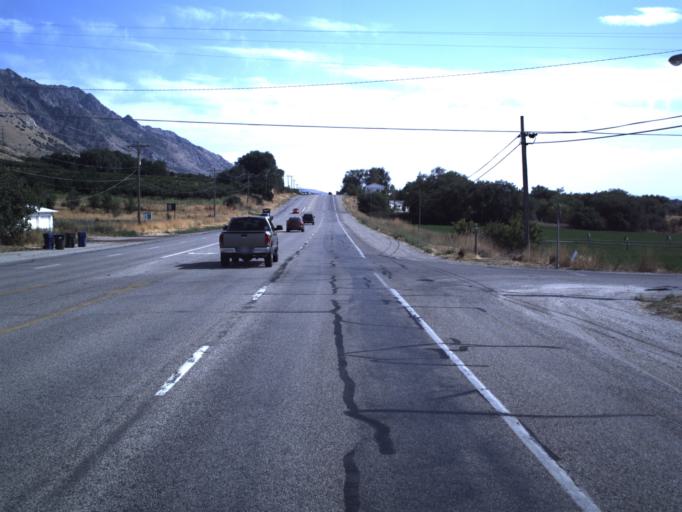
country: US
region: Utah
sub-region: Box Elder County
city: Perry
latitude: 41.4449
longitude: -112.0375
